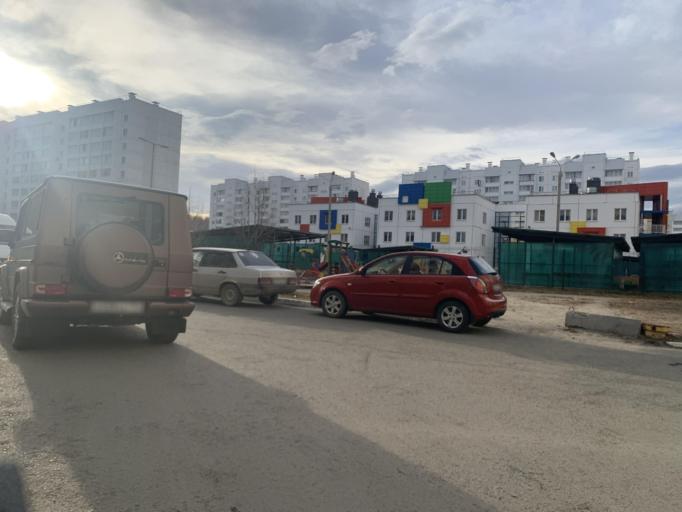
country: RU
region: Chelyabinsk
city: Roshchino
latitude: 55.2075
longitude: 61.3067
